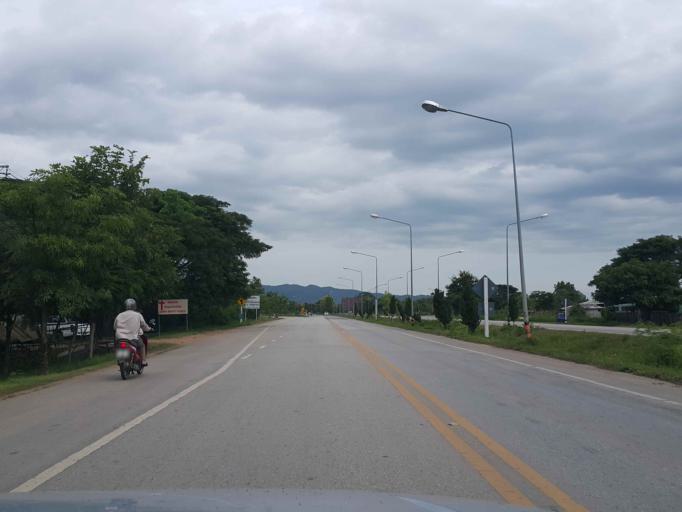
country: TH
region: Lampang
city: Lampang
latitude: 18.2560
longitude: 99.4811
